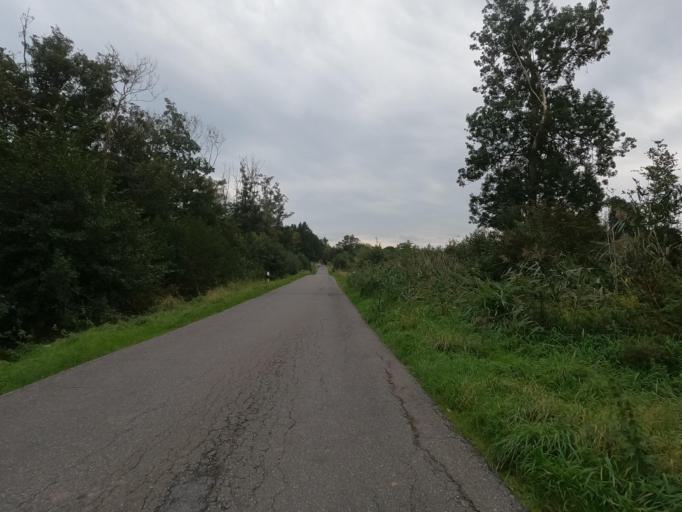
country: DE
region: Schleswig-Holstein
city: Neukirchen
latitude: 54.3028
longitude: 11.0469
